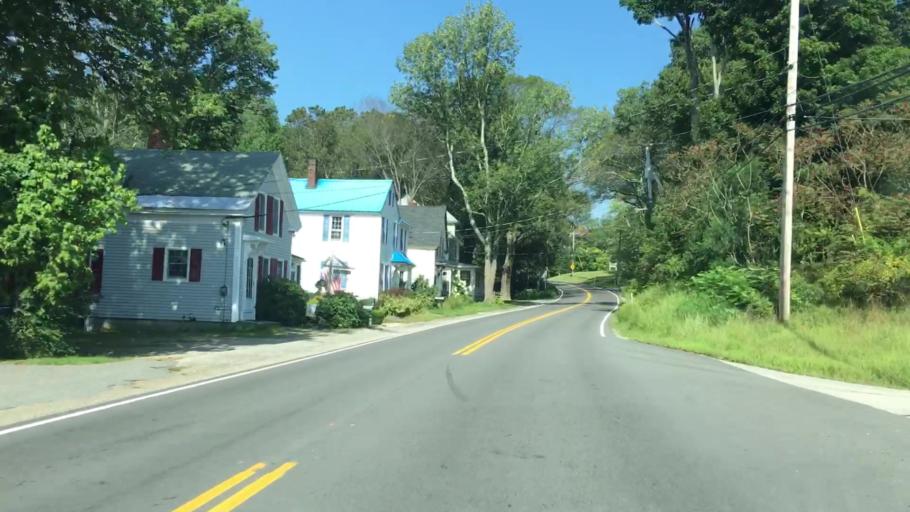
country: US
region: New Hampshire
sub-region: Rockingham County
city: East Kingston
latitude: 42.9235
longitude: -71.0102
